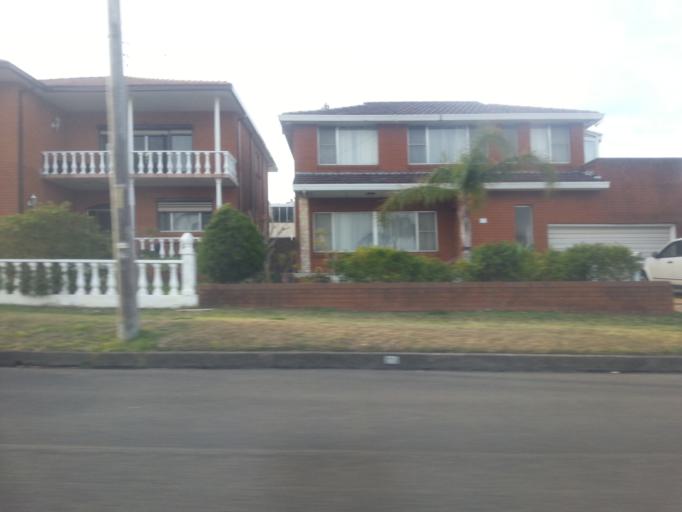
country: AU
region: New South Wales
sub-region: Wollongong
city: Fairy Meadow
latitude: -34.3880
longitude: 150.8841
